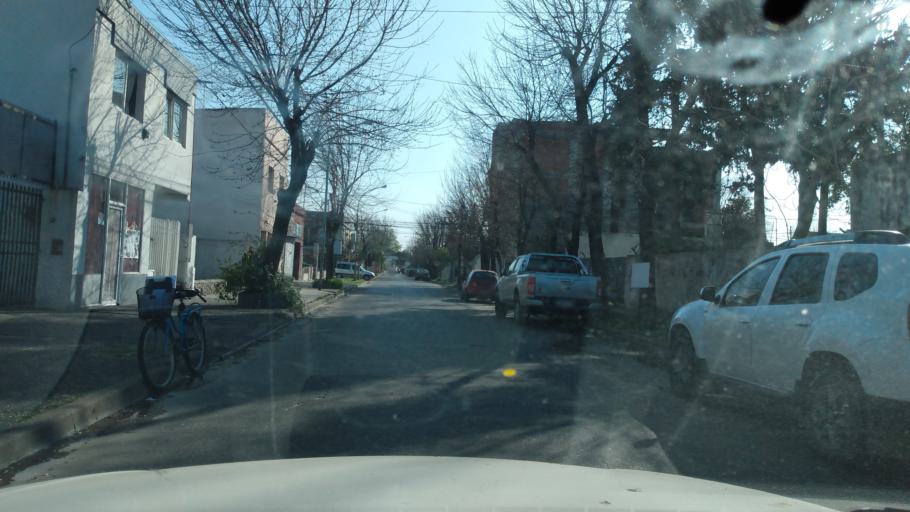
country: AR
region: Buenos Aires
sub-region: Partido de Lujan
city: Lujan
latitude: -34.5623
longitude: -59.1102
